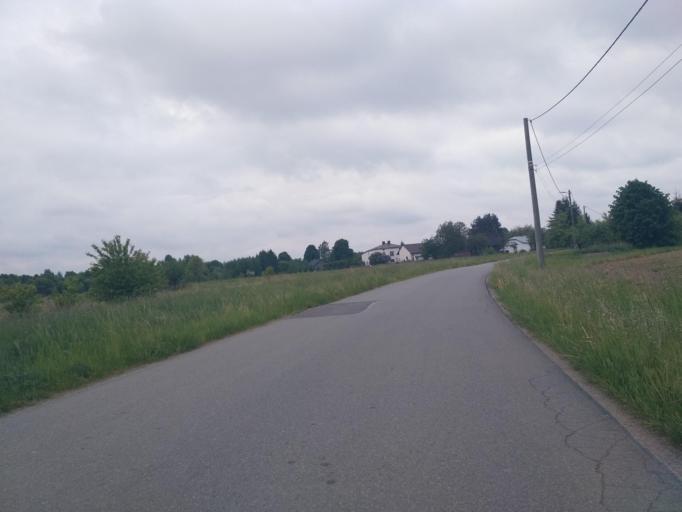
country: PL
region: Subcarpathian Voivodeship
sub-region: Krosno
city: Krosno
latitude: 49.6735
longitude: 21.7322
